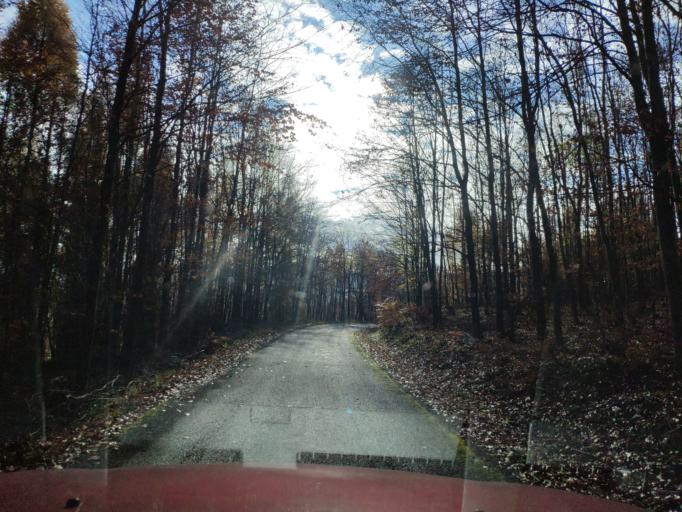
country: SK
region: Kosicky
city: Secovce
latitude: 48.6194
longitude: 21.4612
